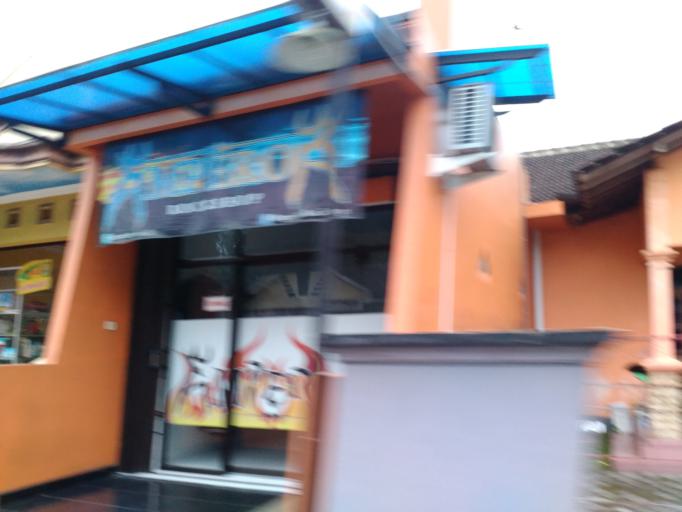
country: ID
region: Central Java
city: Boyolali
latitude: -7.5269
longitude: 110.5936
